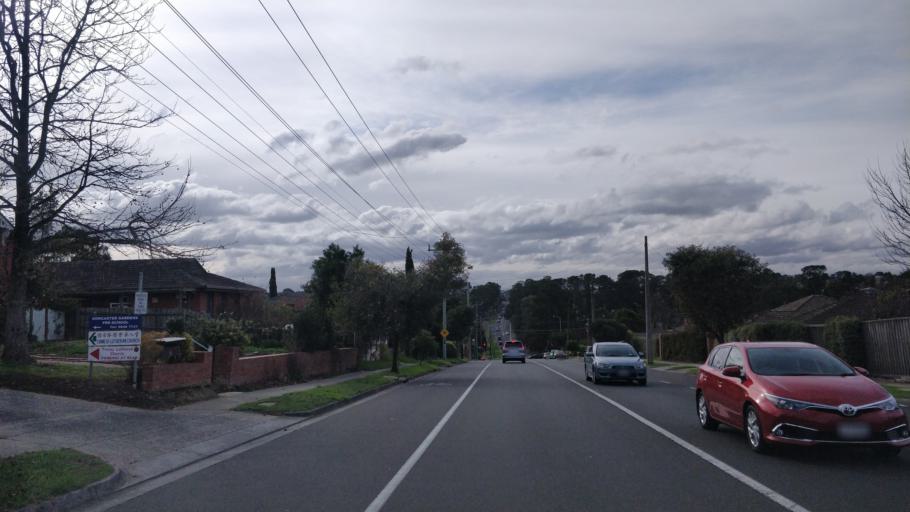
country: AU
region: Victoria
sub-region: Manningham
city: Doncaster East
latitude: -37.7820
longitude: 145.1445
